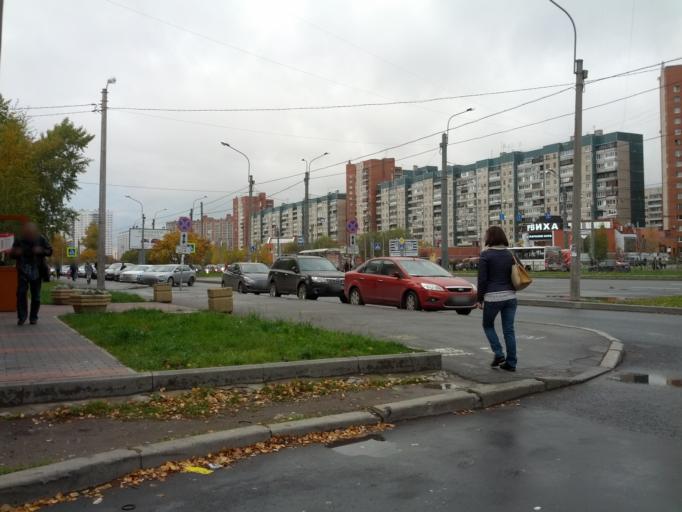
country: RU
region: St.-Petersburg
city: Krasnogvargeisky
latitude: 59.9182
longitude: 30.4651
